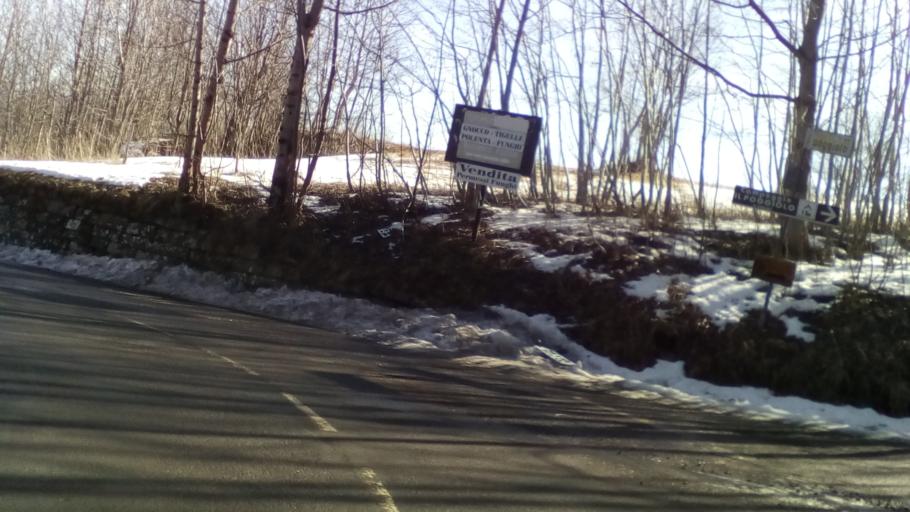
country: IT
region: Emilia-Romagna
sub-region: Provincia di Modena
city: Pievepelago
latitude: 44.1967
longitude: 10.5319
